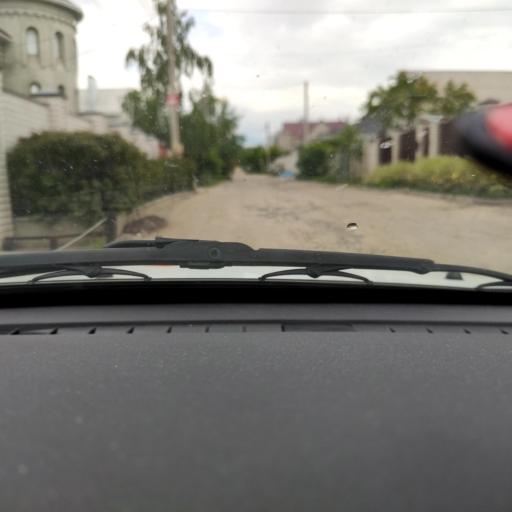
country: RU
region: Voronezj
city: Podgornoye
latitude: 51.7460
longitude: 39.1550
